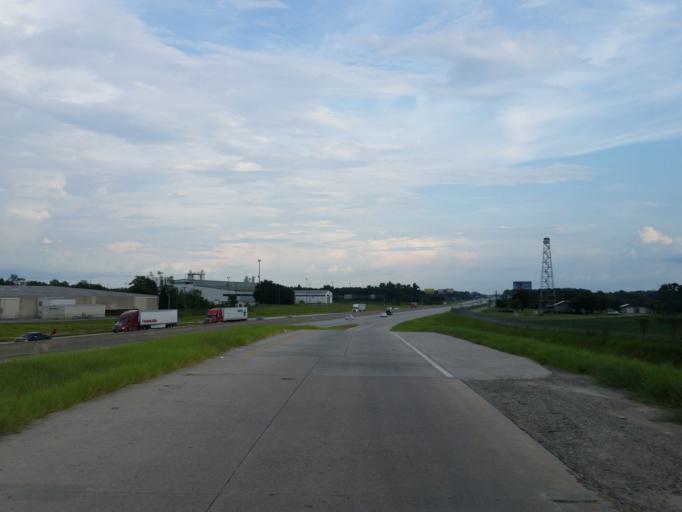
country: US
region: Georgia
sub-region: Cook County
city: Adel
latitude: 31.1120
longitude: -83.4281
